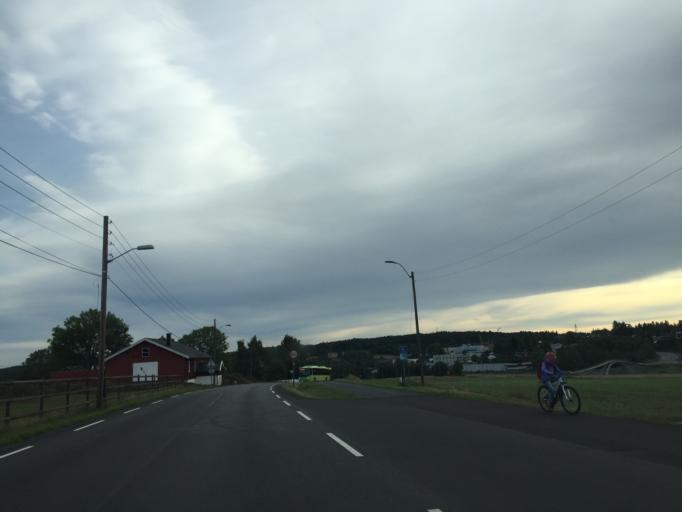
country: NO
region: Akershus
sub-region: As
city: As
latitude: 59.7175
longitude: 10.7767
